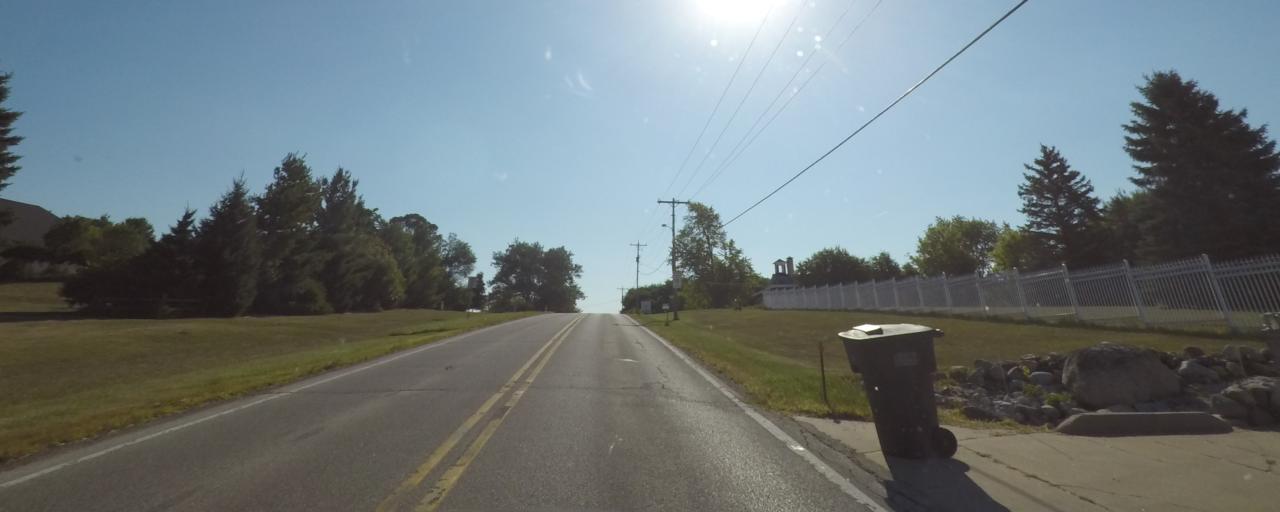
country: US
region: Wisconsin
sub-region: Waukesha County
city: Wales
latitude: 42.9880
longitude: -88.3380
